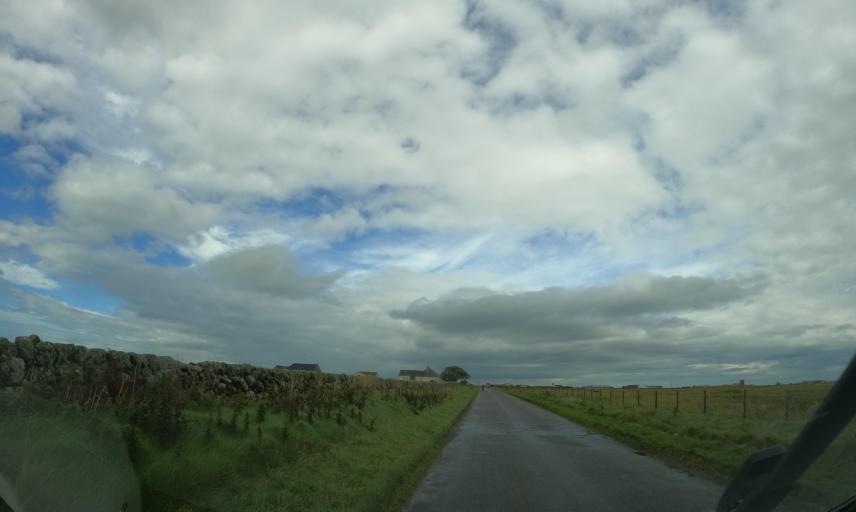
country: GB
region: Scotland
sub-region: Eilean Siar
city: Barra
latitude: 56.4917
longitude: -6.8824
